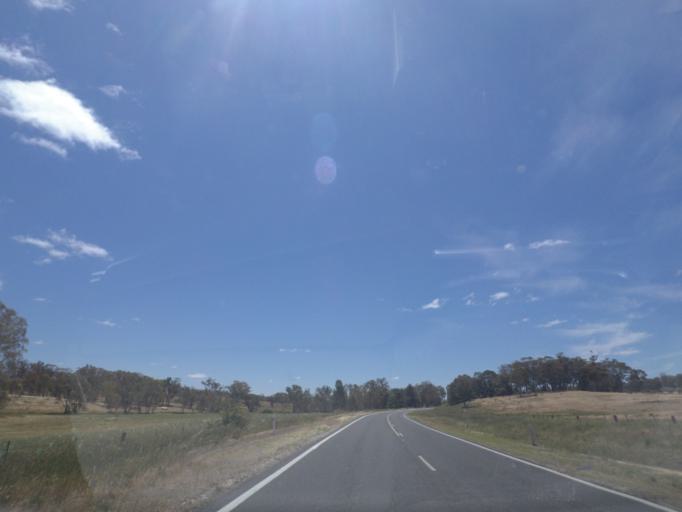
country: AU
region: Victoria
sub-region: Mount Alexander
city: Castlemaine
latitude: -37.1728
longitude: 144.1462
